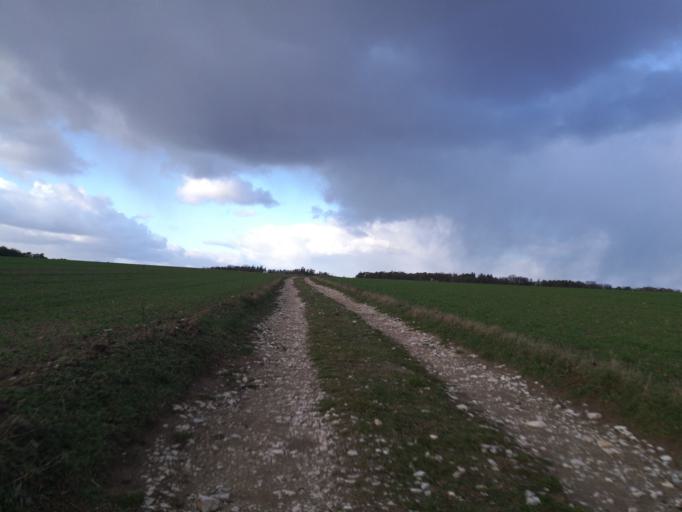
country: DE
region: Bavaria
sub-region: Regierungsbezirk Mittelfranken
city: Obermichelbach
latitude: 49.4968
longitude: 10.9258
